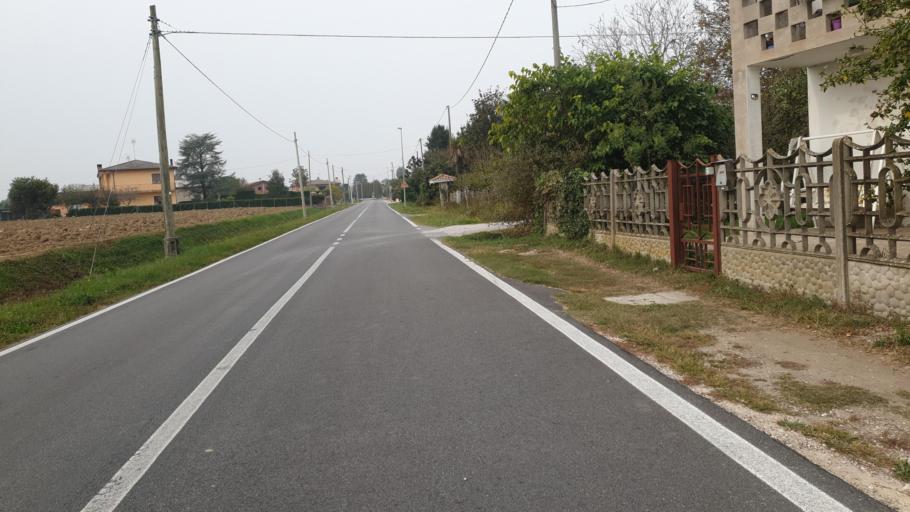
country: IT
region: Veneto
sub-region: Provincia di Padova
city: Bertipaglia
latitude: 45.3056
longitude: 11.8976
